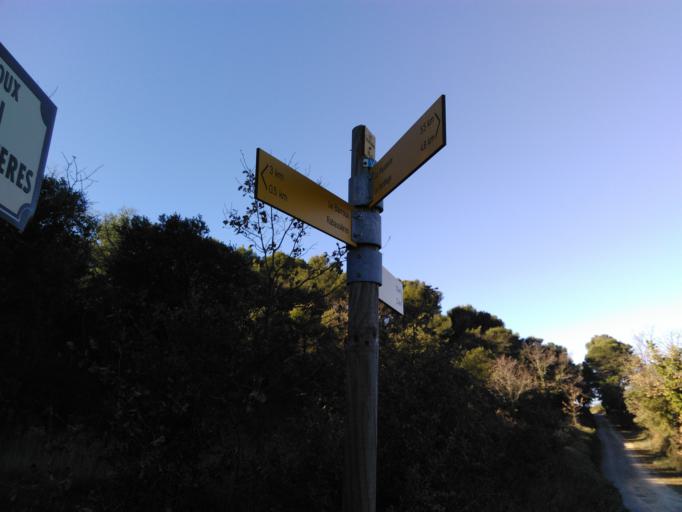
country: FR
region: Provence-Alpes-Cote d'Azur
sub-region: Departement du Vaucluse
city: Malaucene
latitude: 44.1590
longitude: 5.0922
